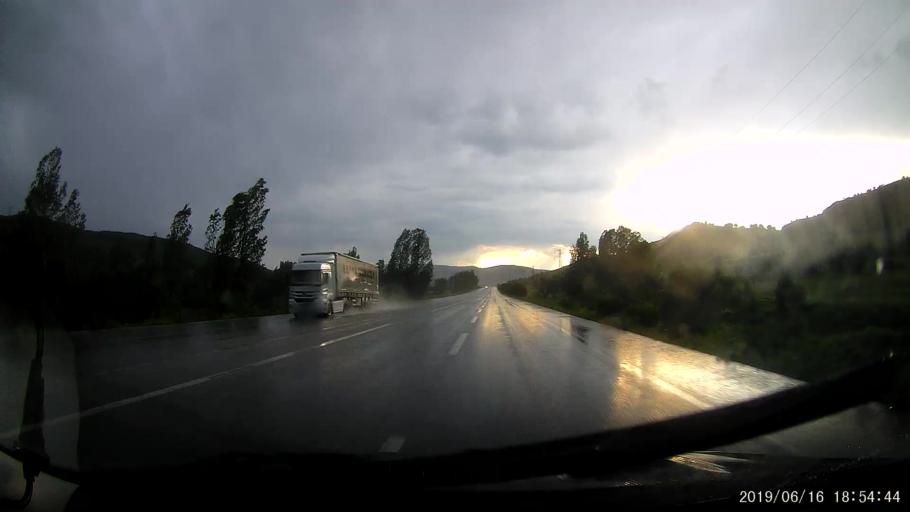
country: TR
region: Erzincan
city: Catalcam
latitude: 39.8976
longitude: 38.8459
